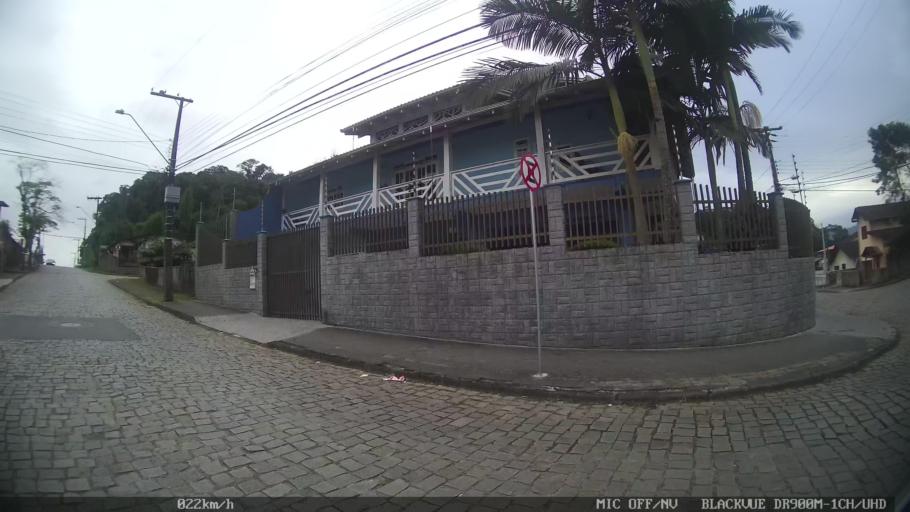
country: BR
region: Santa Catarina
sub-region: Joinville
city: Joinville
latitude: -26.2813
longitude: -48.8822
